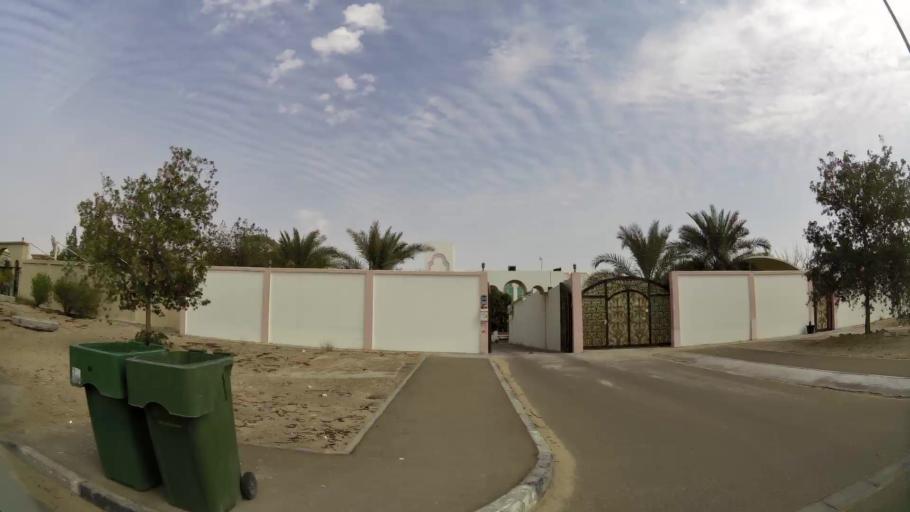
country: AE
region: Abu Dhabi
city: Abu Dhabi
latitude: 24.5531
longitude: 54.6859
